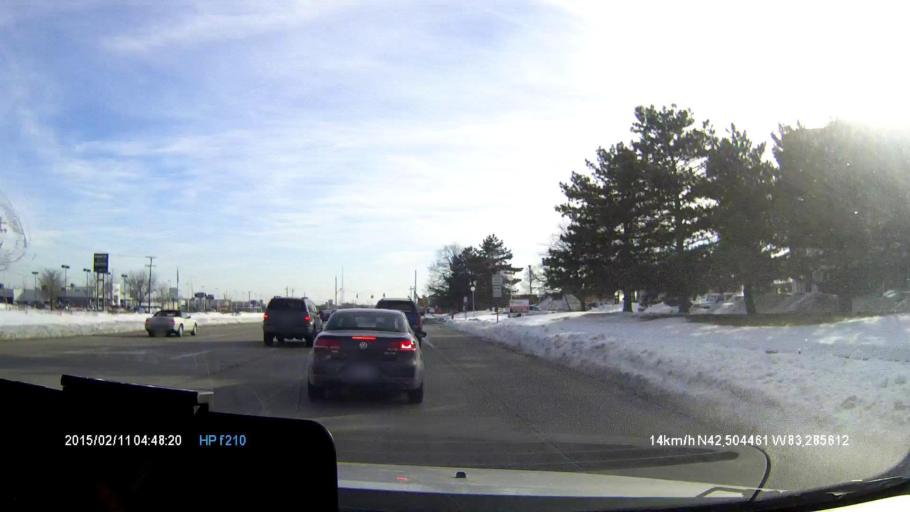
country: US
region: Michigan
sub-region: Oakland County
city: Bingham Farms
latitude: 42.5042
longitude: -83.2856
